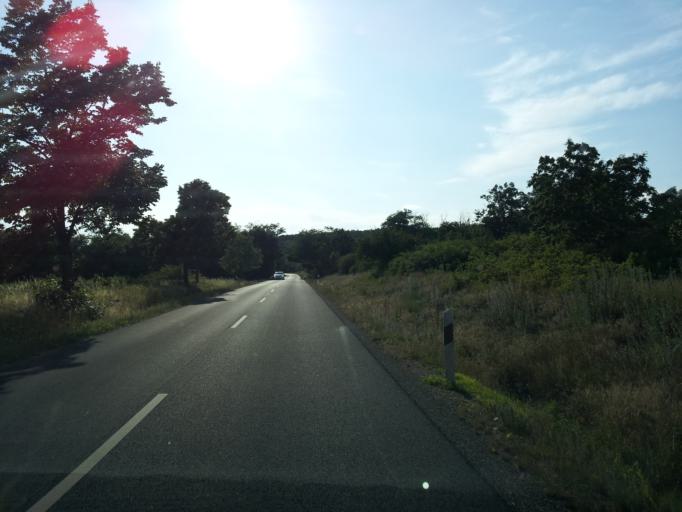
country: HU
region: Veszprem
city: Urkut
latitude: 47.0033
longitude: 17.6340
